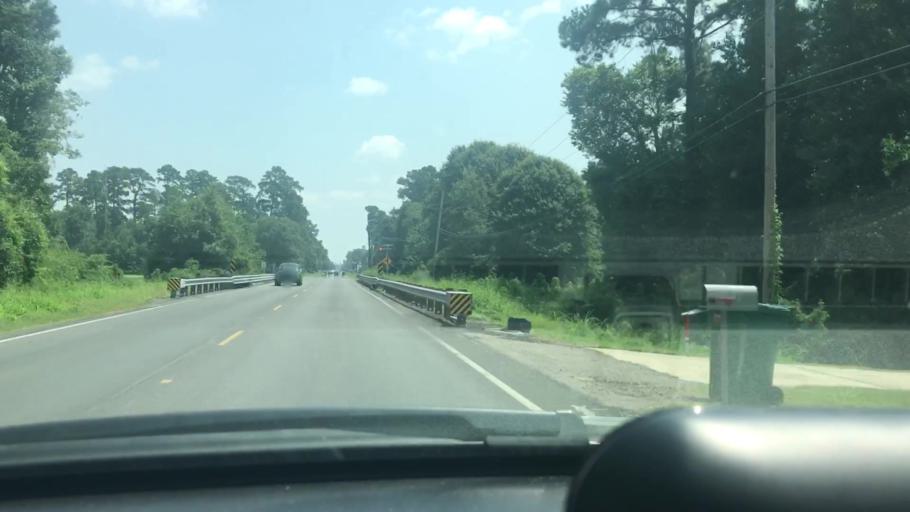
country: US
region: Louisiana
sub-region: Livingston Parish
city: Walker
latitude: 30.4849
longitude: -90.8937
